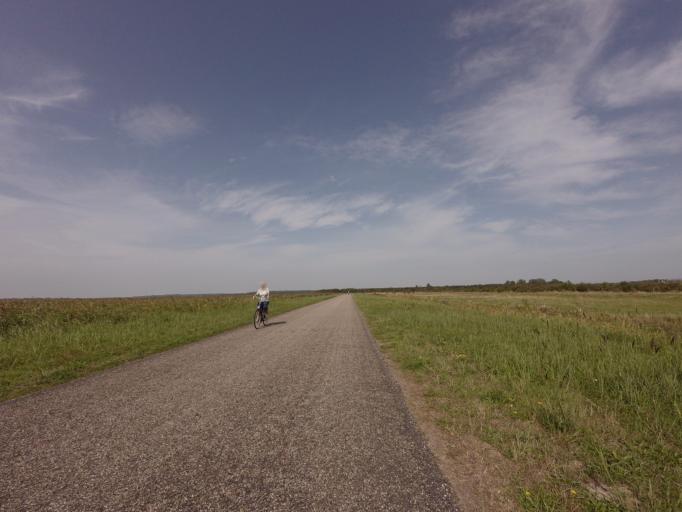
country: NL
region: Groningen
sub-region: Gemeente De Marne
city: Ulrum
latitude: 53.3513
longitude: 6.2660
